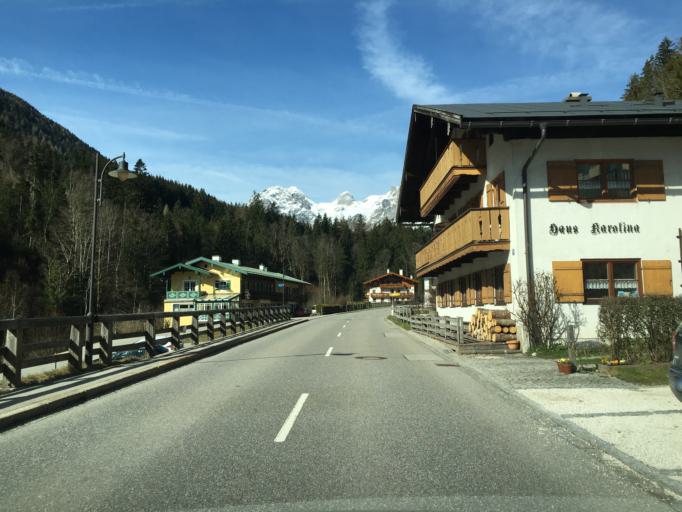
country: DE
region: Bavaria
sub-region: Upper Bavaria
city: Ramsau
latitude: 47.6072
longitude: 12.8914
